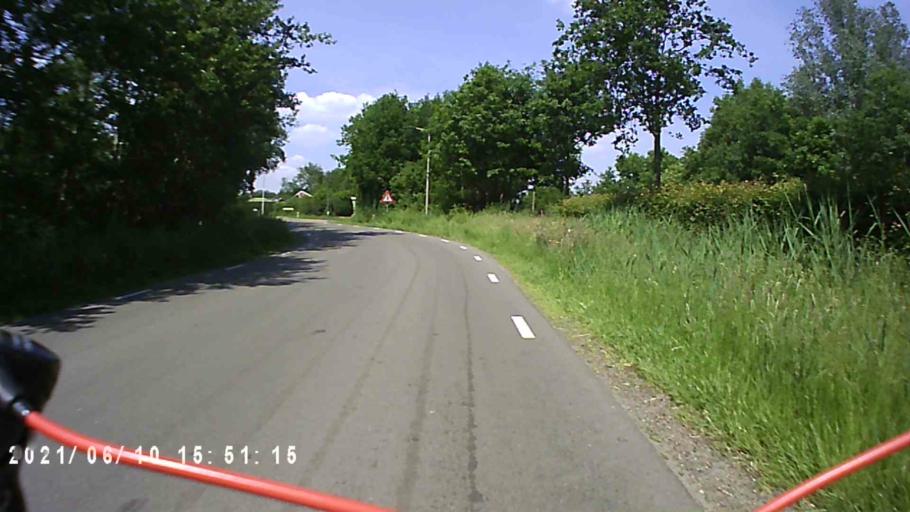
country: NL
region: Friesland
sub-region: Gemeente Achtkarspelen
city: Harkema
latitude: 53.1723
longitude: 6.1183
